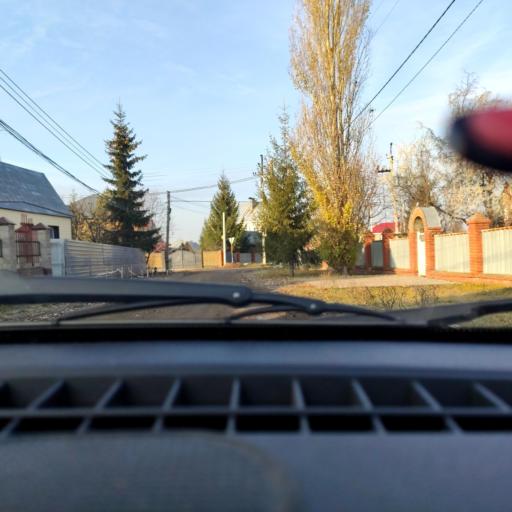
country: RU
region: Bashkortostan
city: Ufa
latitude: 54.6109
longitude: 55.9320
